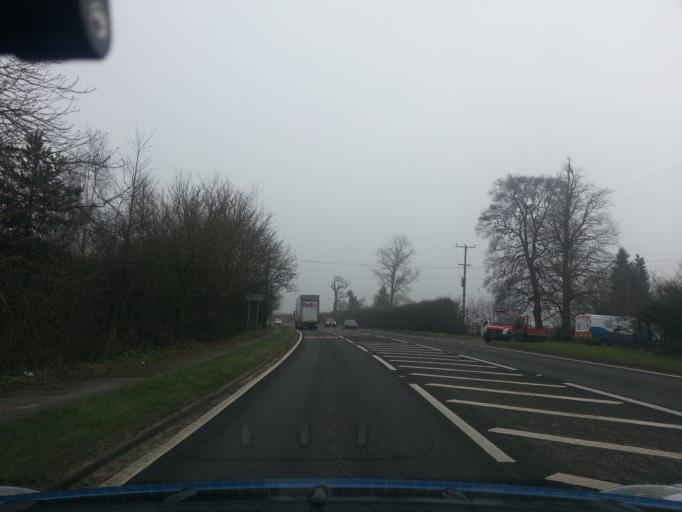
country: GB
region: England
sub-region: Oxfordshire
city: Marcham
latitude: 51.7075
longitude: -1.3388
